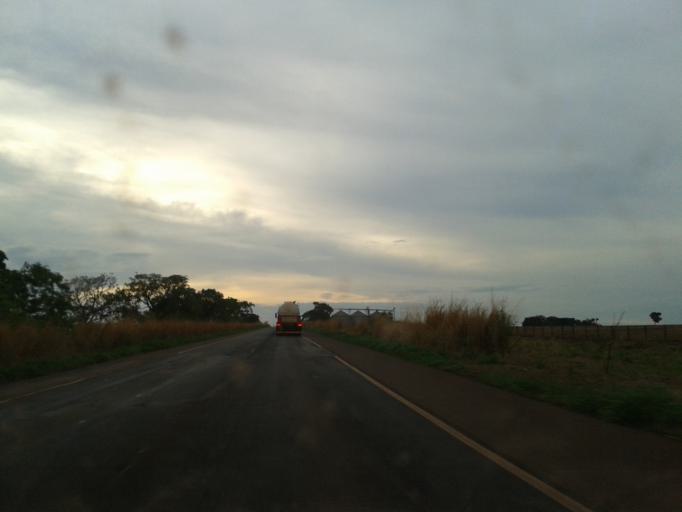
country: BR
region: Goias
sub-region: Santa Helena De Goias
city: Santa Helena de Goias
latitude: -17.9387
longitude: -50.5324
